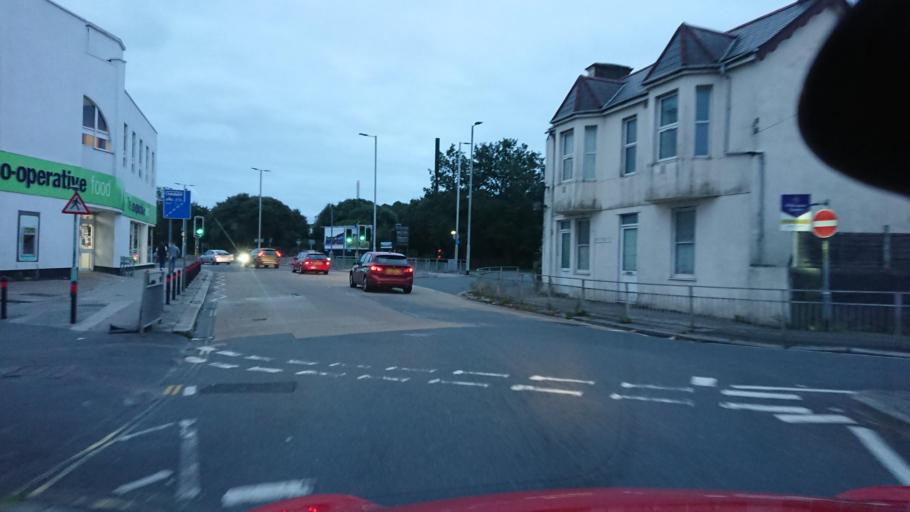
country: GB
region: England
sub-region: Cornwall
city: Torpoint
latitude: 50.4028
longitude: -4.1873
